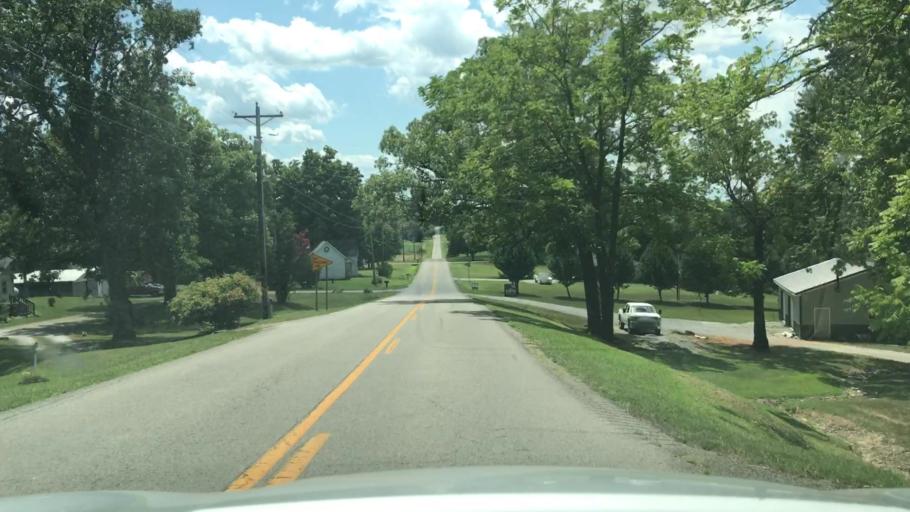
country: US
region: Kentucky
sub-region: Muhlenberg County
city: Greenville
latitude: 37.1628
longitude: -87.2501
